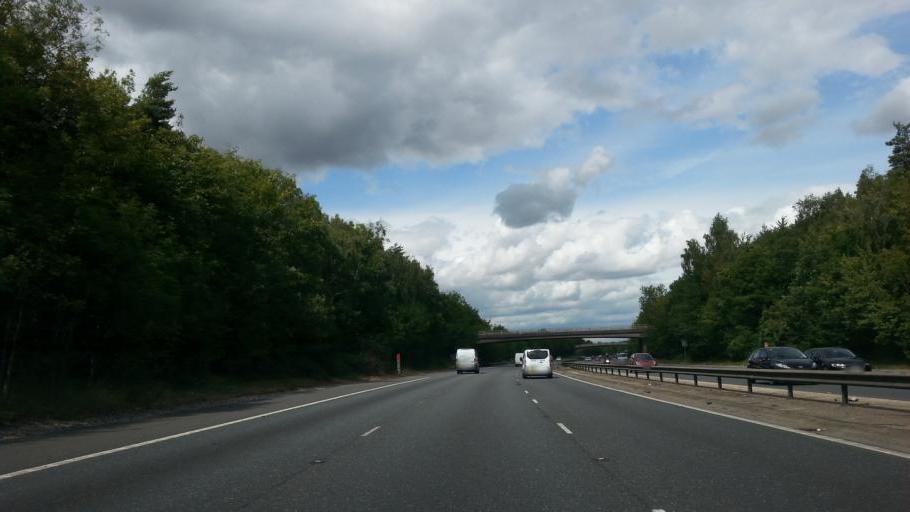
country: GB
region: England
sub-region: Essex
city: Little Hallingbury
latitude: 51.8485
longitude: 0.1851
